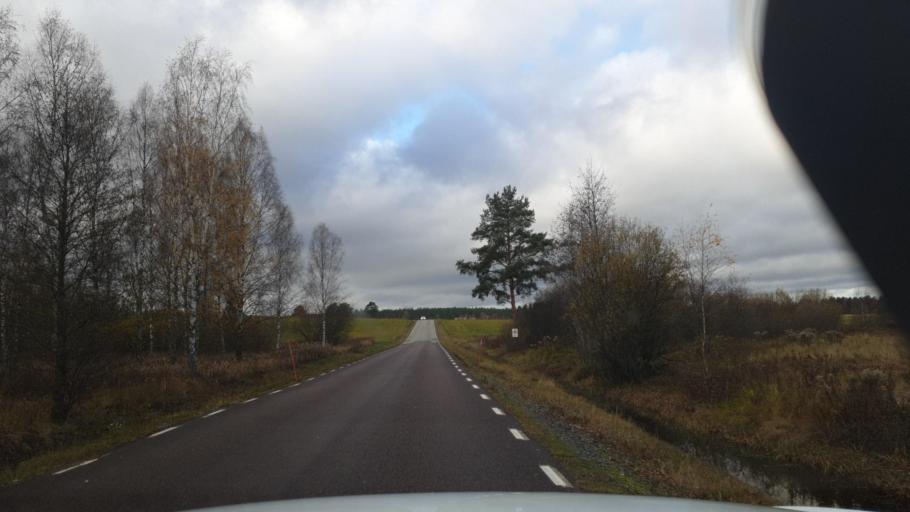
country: SE
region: Vaermland
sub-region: Arvika Kommun
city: Arvika
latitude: 59.5186
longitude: 12.8418
